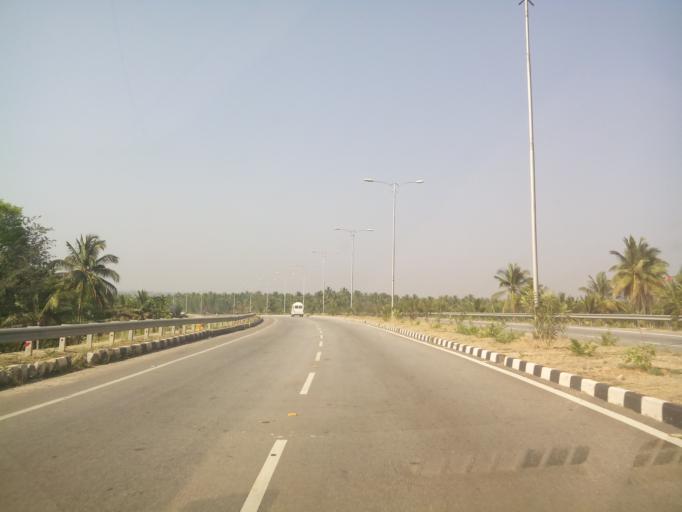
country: IN
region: Karnataka
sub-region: Tumkur
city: Kunigal
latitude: 13.0290
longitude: 77.0772
